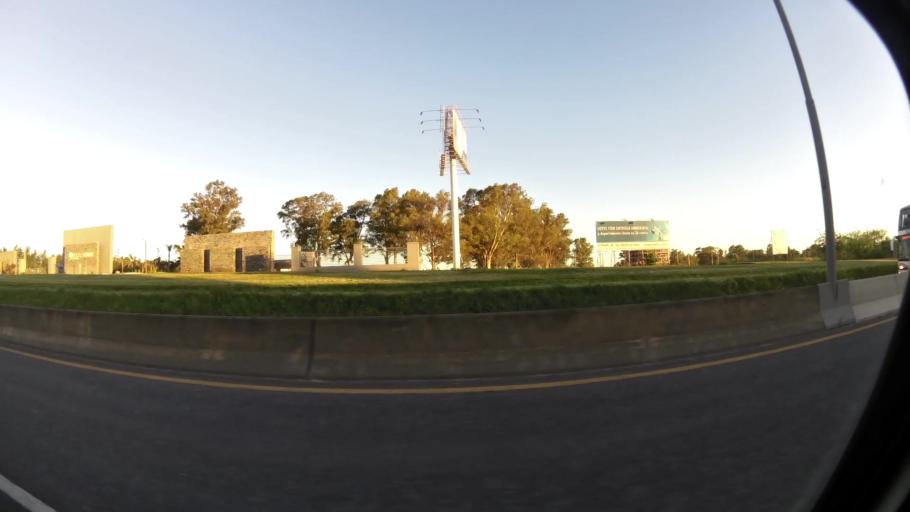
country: AR
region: Buenos Aires
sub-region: Partido de Quilmes
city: Quilmes
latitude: -34.8081
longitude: -58.1729
